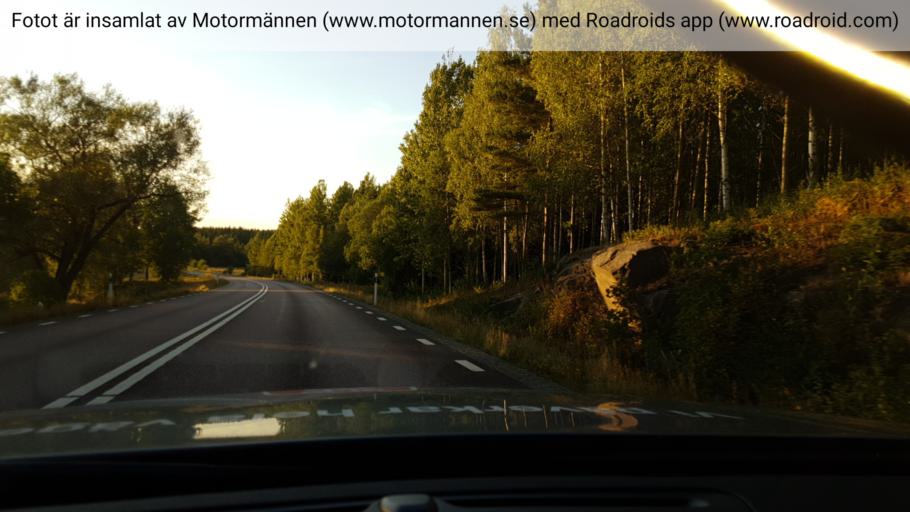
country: SE
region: OErebro
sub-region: Karlskoga Kommun
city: Karlskoga
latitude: 59.4255
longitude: 14.4264
